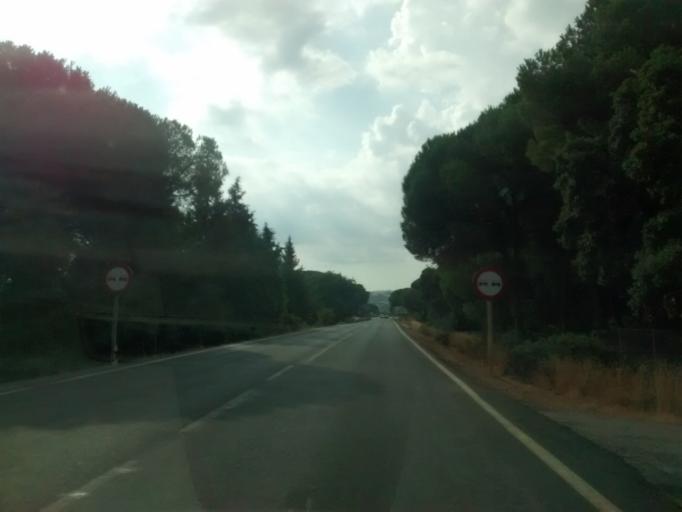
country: ES
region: Andalusia
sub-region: Provincia de Cadiz
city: Arcos de la Frontera
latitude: 36.7500
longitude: -5.7753
